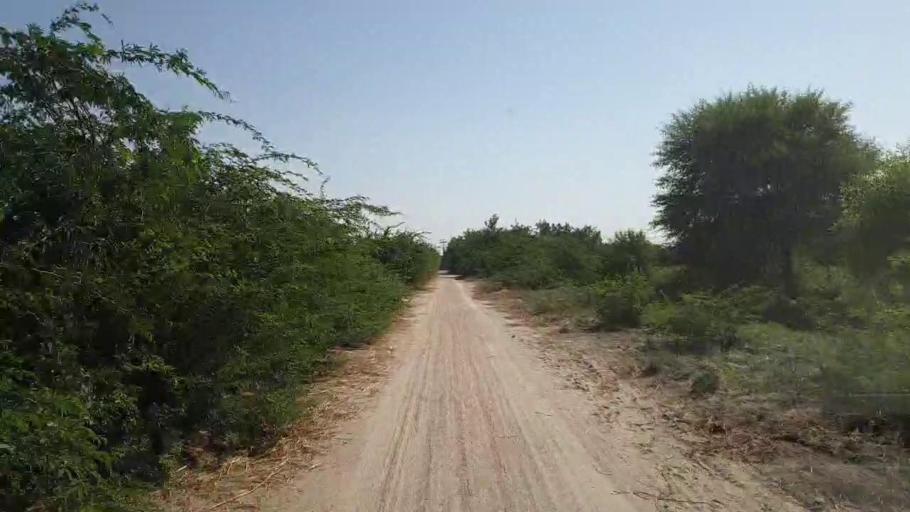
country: PK
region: Sindh
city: Tando Bago
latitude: 24.6471
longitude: 68.9857
